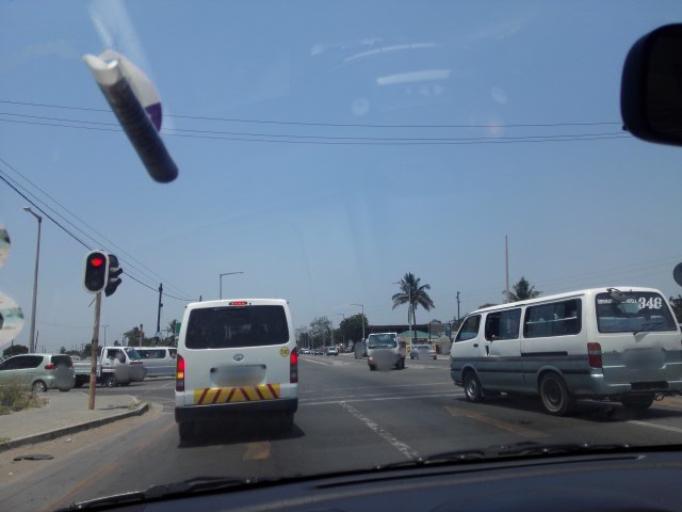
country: MZ
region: Maputo City
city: Maputo
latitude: -25.9217
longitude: 32.5624
